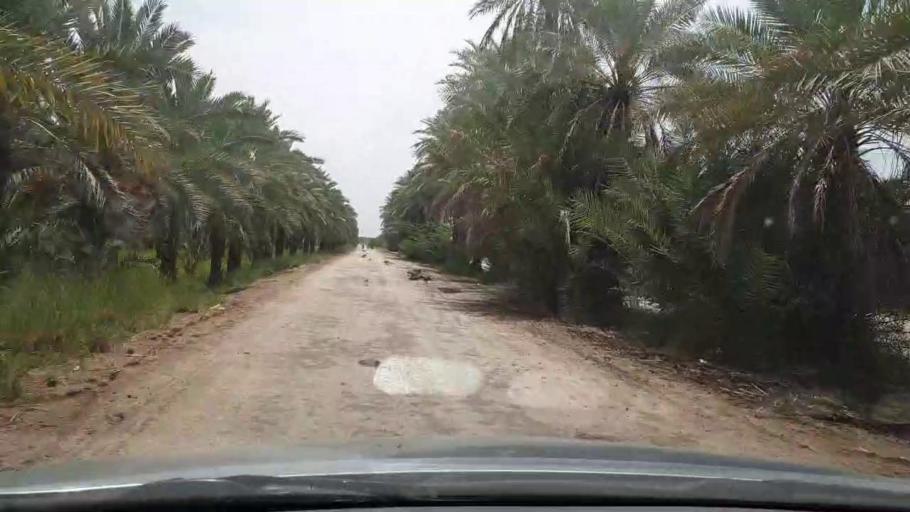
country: PK
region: Sindh
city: Khairpur
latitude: 27.4273
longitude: 68.7810
